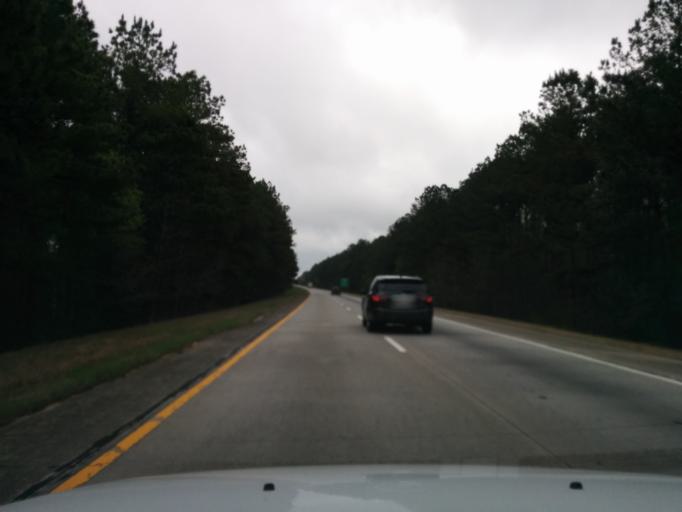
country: US
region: Georgia
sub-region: Candler County
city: Metter
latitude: 32.3774
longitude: -82.1944
